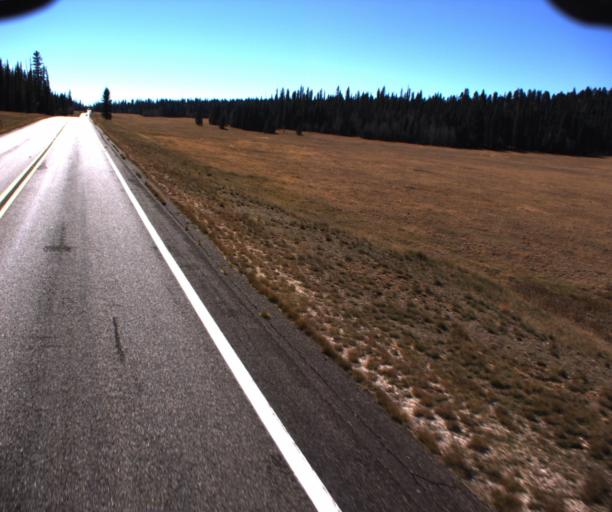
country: US
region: Arizona
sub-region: Coconino County
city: Grand Canyon
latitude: 36.3497
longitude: -112.1179
